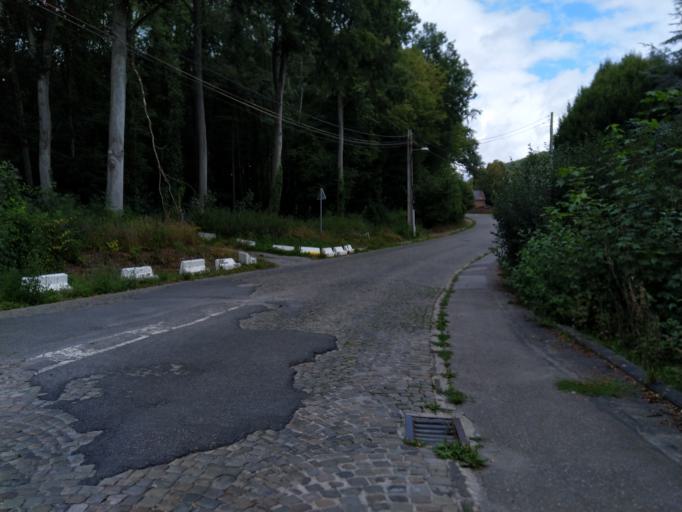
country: BE
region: Wallonia
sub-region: Province du Hainaut
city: Thuin
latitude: 50.3827
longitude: 4.3465
